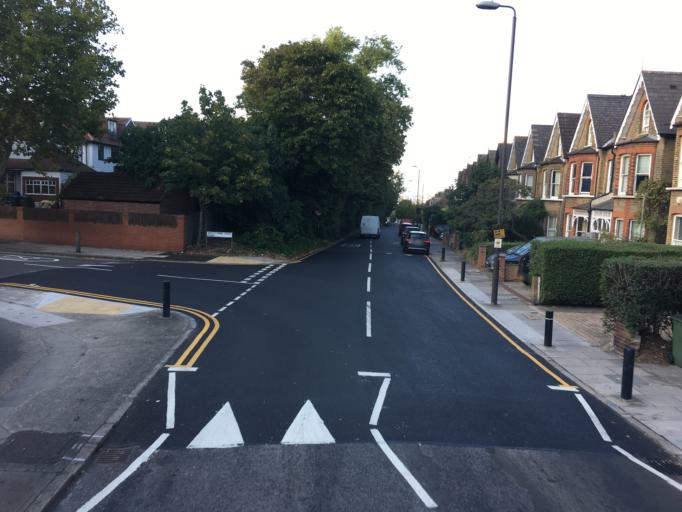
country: GB
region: England
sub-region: Greater London
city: Blackheath
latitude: 51.4785
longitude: 0.0192
